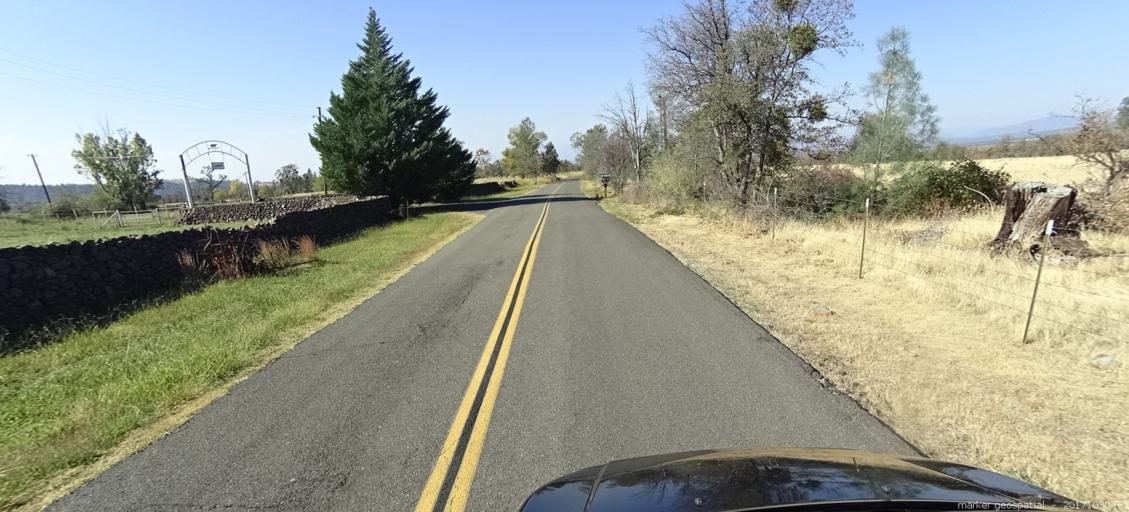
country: US
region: California
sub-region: Shasta County
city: Shingletown
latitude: 40.6378
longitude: -121.9580
